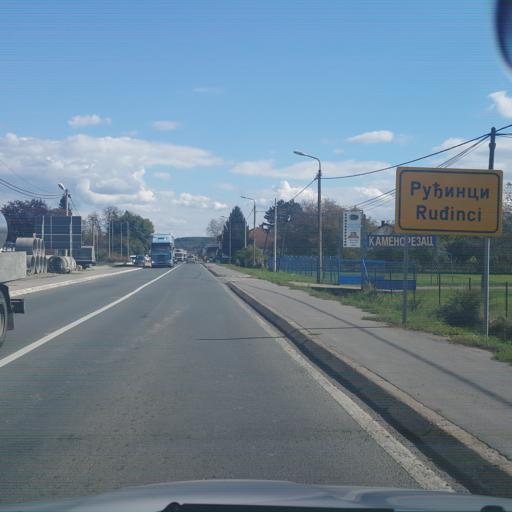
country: RS
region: Central Serbia
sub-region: Raski Okrug
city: Vrnjacka Banja
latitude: 43.6395
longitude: 20.9227
